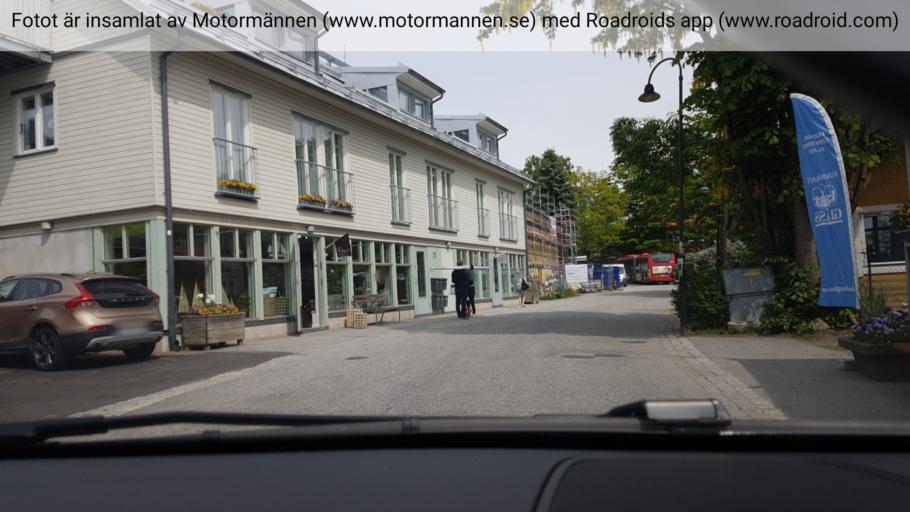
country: SE
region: Stockholm
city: Dalaro
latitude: 59.1322
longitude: 18.4073
